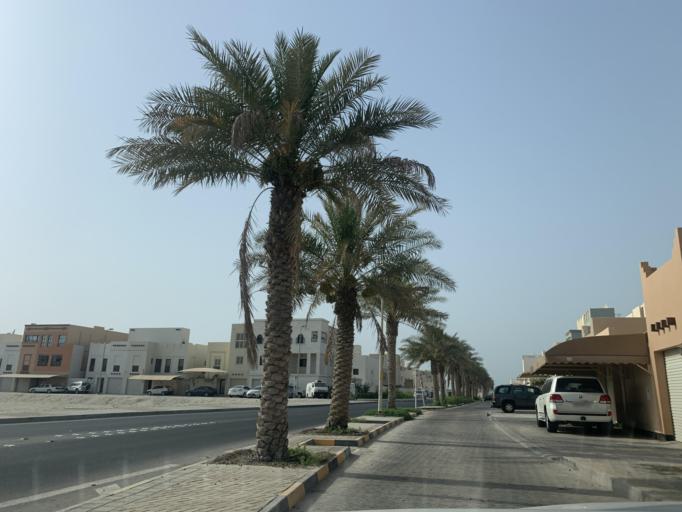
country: BH
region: Manama
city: Jidd Hafs
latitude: 26.2248
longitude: 50.4417
